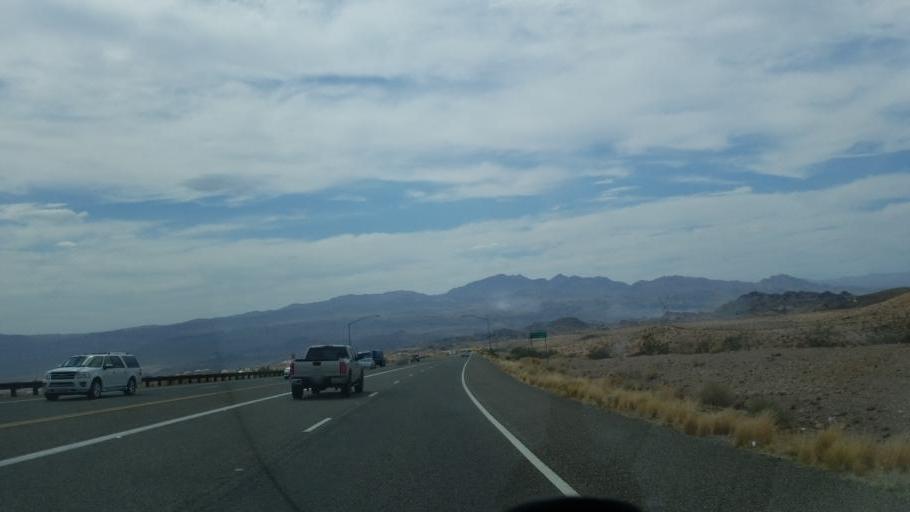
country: US
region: Nevada
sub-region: Clark County
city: Laughlin
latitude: 35.1857
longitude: -114.4985
